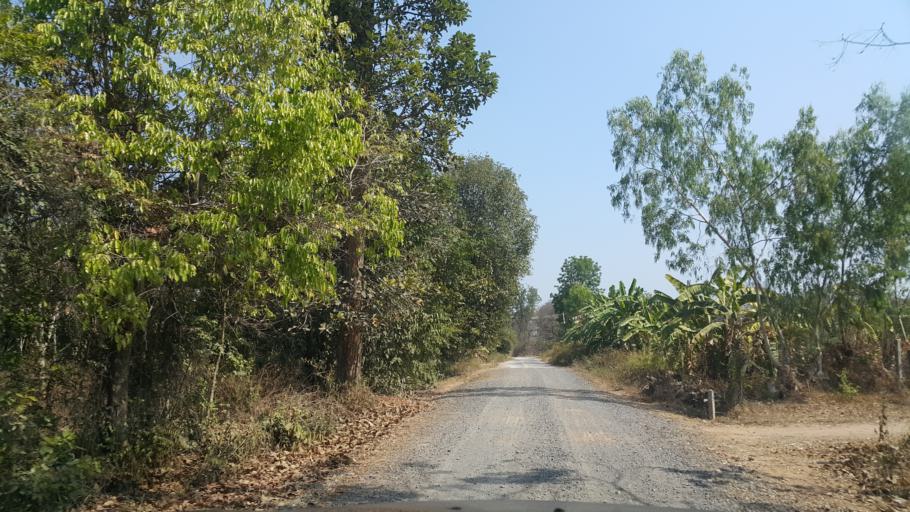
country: TH
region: Buriram
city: Krasang
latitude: 15.1034
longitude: 103.3747
